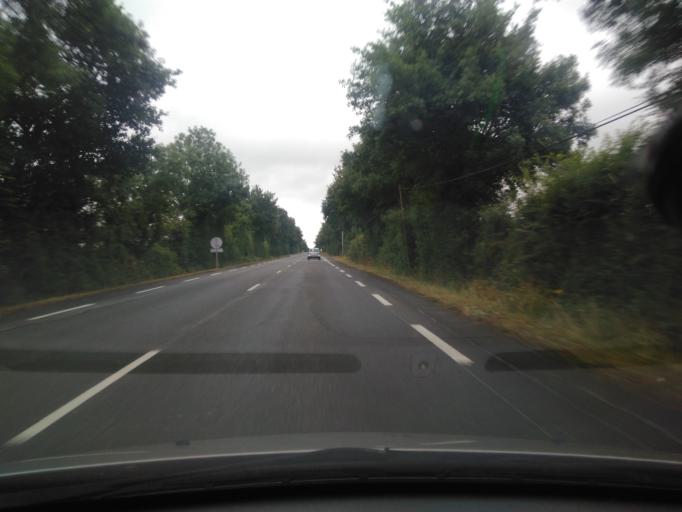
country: FR
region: Pays de la Loire
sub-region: Departement de la Vendee
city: Saint-Florent-des-Bois
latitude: 46.6145
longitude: -1.3532
